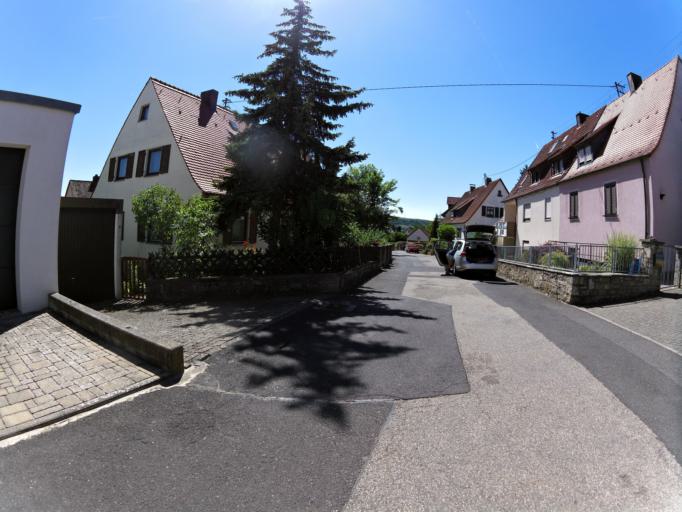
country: DE
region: Bavaria
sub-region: Regierungsbezirk Unterfranken
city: Ochsenfurt
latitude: 49.6718
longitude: 10.0600
